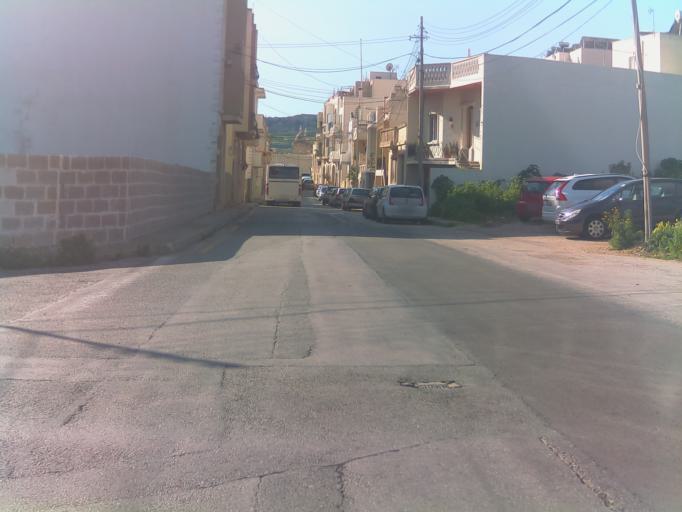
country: MT
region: L-Imgarr
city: Imgarr
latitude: 35.9236
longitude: 14.3672
